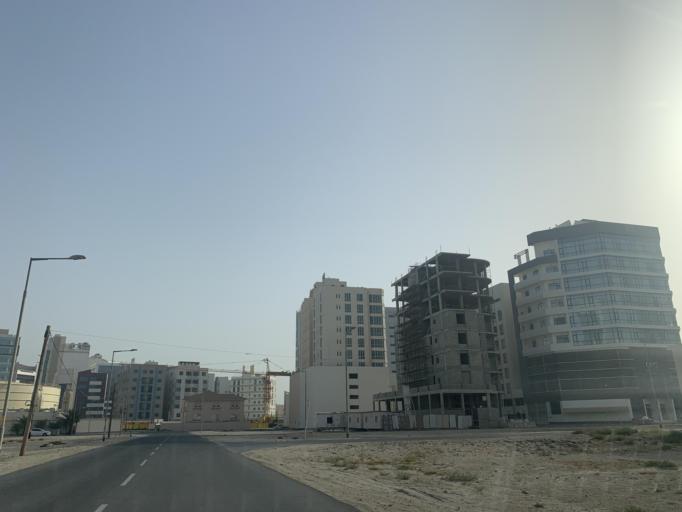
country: BH
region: Manama
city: Jidd Hafs
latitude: 26.2409
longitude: 50.5326
